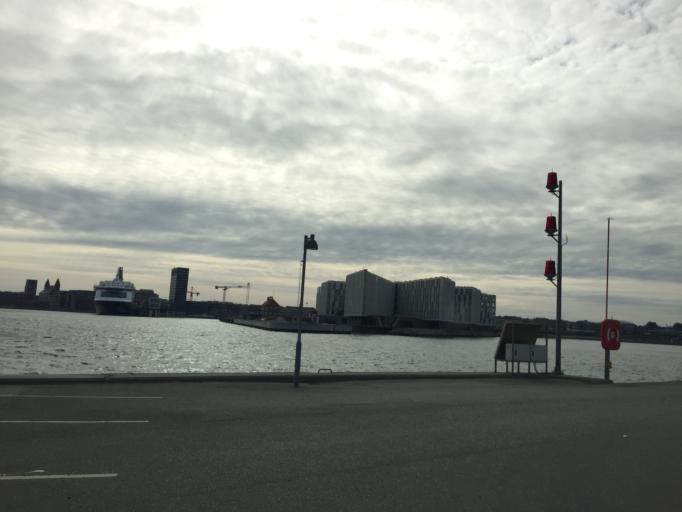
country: DK
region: Capital Region
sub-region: Kobenhavn
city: Christianshavn
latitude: 55.7064
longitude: 12.6025
